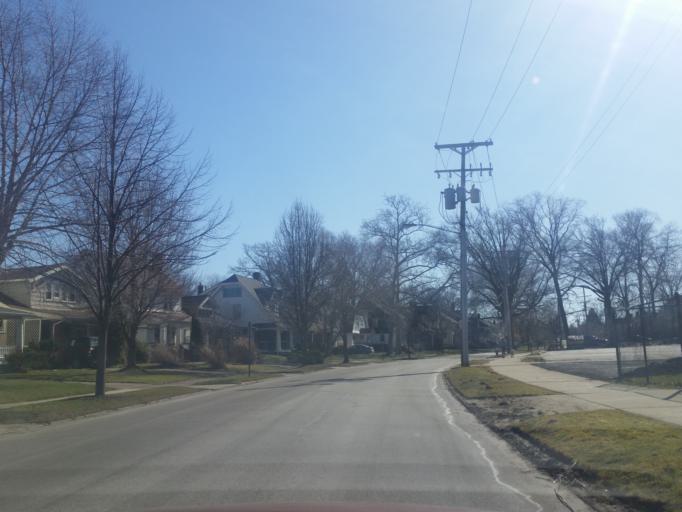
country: US
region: Ohio
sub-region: Cuyahoga County
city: Lakewood
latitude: 41.4807
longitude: -81.7853
